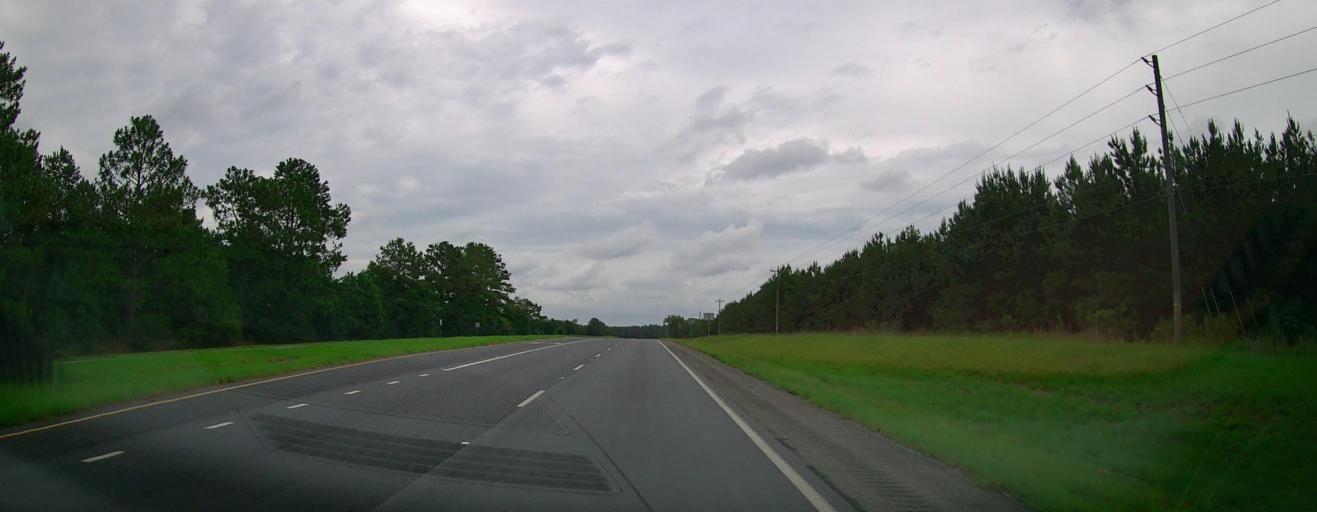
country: US
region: Georgia
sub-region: Dodge County
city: Eastman
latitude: 32.1139
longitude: -83.1011
